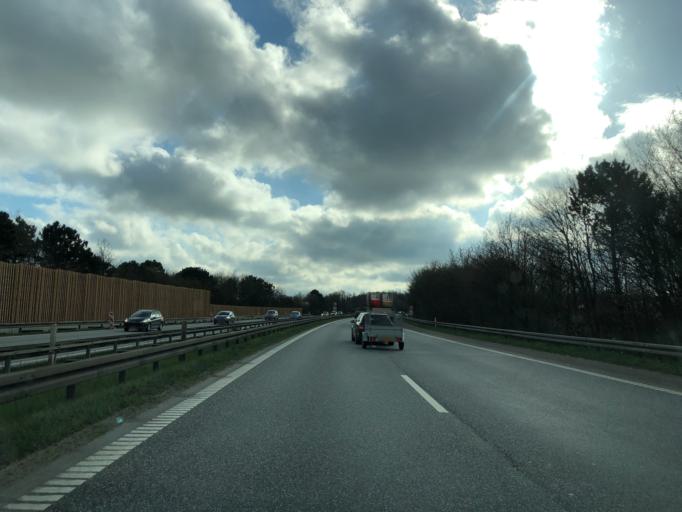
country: DK
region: North Denmark
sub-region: Alborg Kommune
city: Gistrup
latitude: 57.0166
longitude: 9.9549
